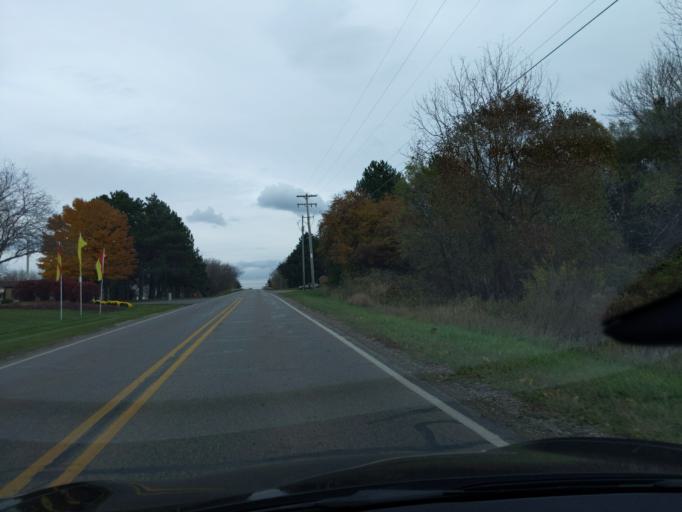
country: US
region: Michigan
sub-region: Ingham County
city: East Lansing
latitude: 42.7841
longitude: -84.5188
